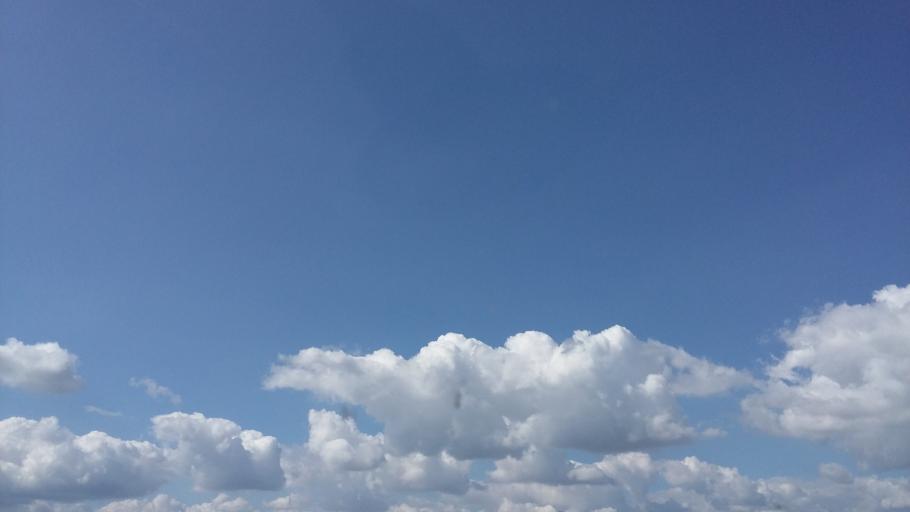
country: DE
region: Bavaria
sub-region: Swabia
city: Holzheim
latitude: 48.3656
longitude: 10.0689
